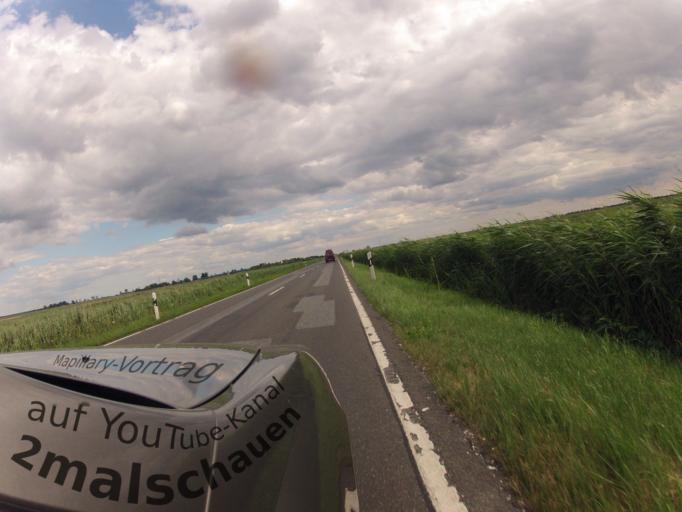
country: DE
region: Mecklenburg-Vorpommern
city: Lassan
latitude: 53.8700
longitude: 13.8138
